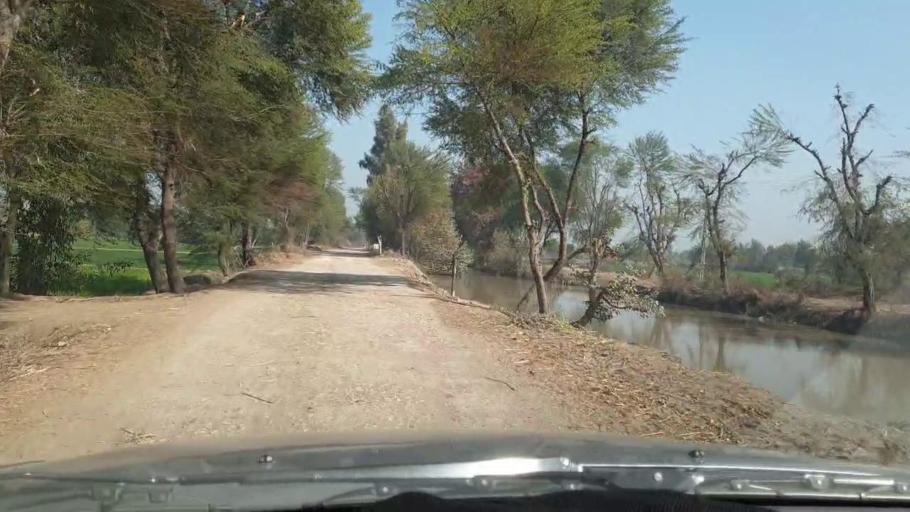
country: PK
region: Sindh
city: Khanpur
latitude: 27.7817
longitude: 69.5450
